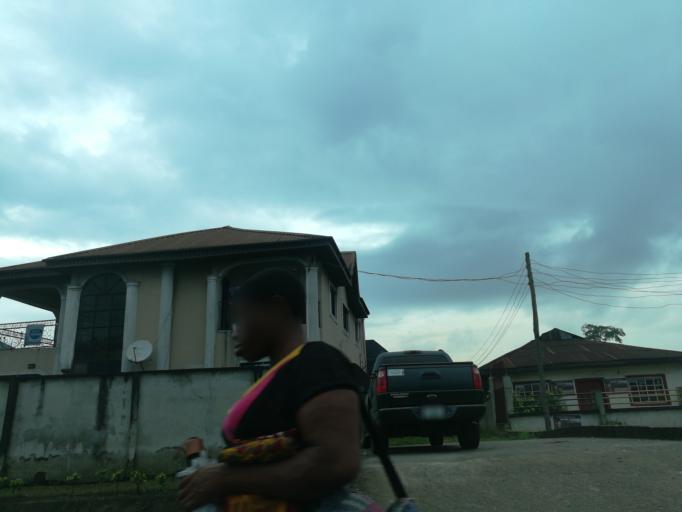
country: NG
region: Rivers
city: Port Harcourt
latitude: 4.8193
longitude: 7.0160
